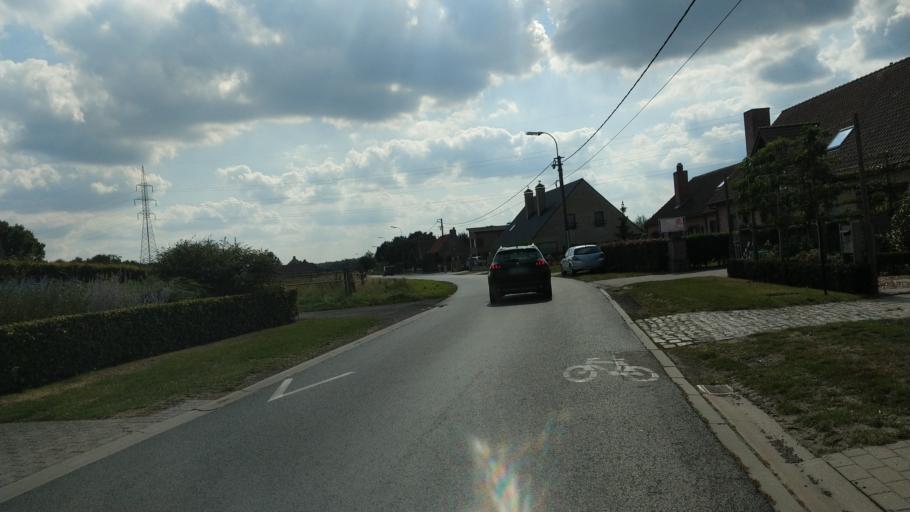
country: BE
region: Flanders
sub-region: Provincie Oost-Vlaanderen
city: Kaprijke
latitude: 51.1850
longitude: 3.6802
